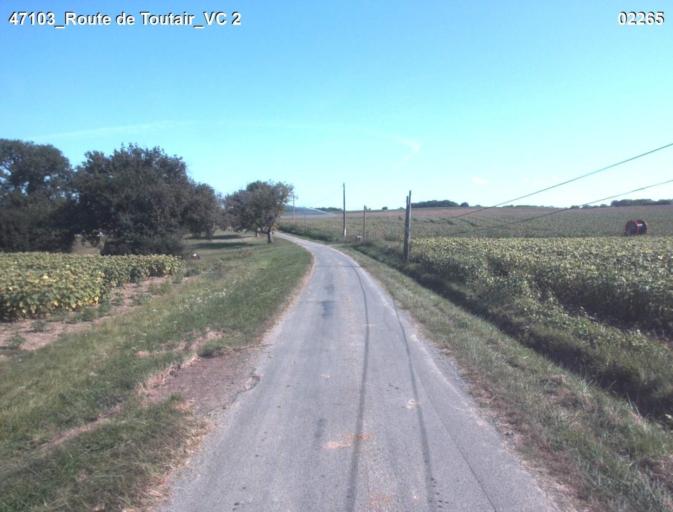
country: FR
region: Aquitaine
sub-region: Departement du Lot-et-Garonne
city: Nerac
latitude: 44.0689
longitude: 0.3338
